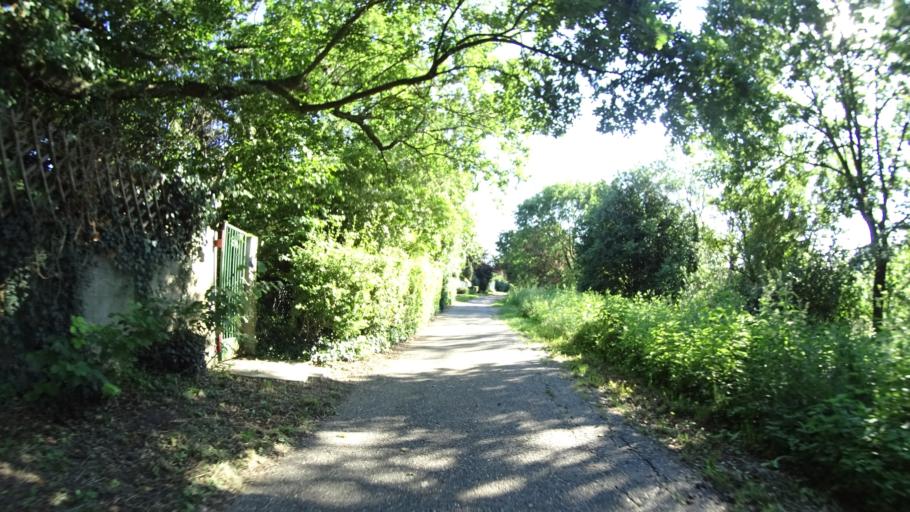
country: DE
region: Baden-Wuerttemberg
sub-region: Karlsruhe Region
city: Eggenstein-Leopoldshafen
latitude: 49.0846
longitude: 8.3946
